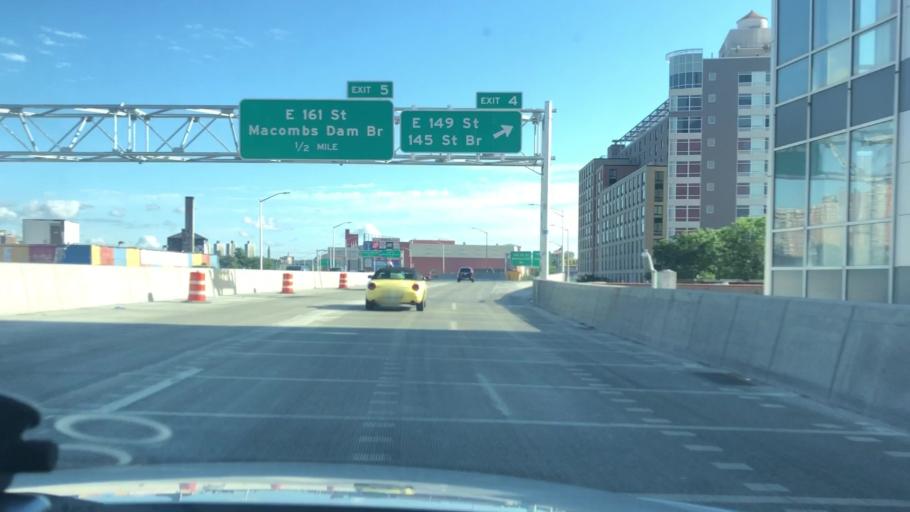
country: US
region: New Jersey
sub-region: Bergen County
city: Edgewater
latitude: 40.8170
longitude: -73.9309
